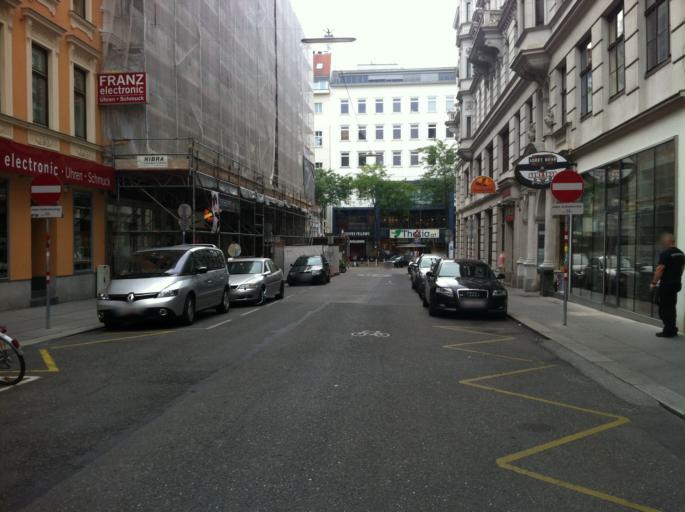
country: AT
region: Vienna
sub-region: Wien Stadt
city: Vienna
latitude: 48.1977
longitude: 16.3457
